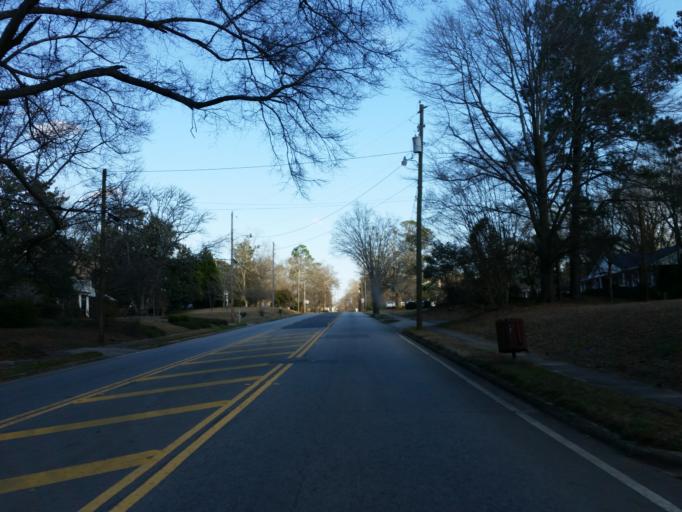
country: US
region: Georgia
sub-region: Monroe County
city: Forsyth
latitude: 33.0345
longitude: -83.9500
